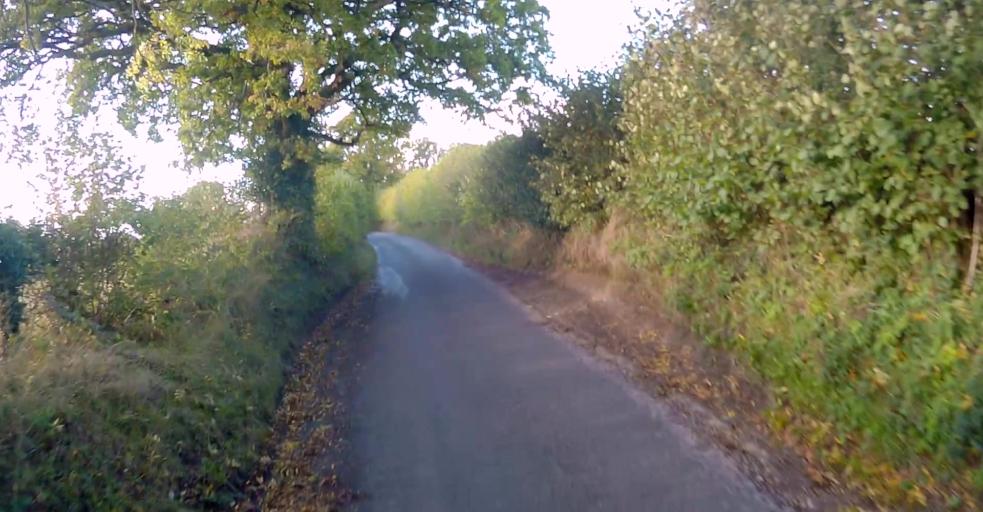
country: GB
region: England
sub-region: Hampshire
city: Long Sutton
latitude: 51.2112
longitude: -0.9067
